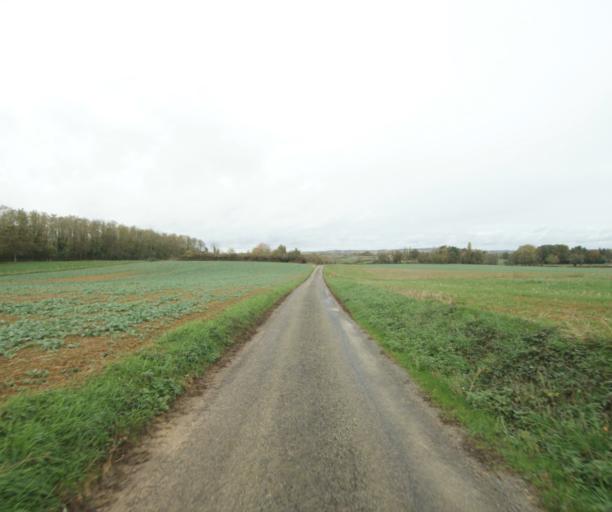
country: FR
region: Rhone-Alpes
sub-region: Departement de l'Ain
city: Pont-de-Vaux
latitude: 46.4559
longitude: 4.8810
